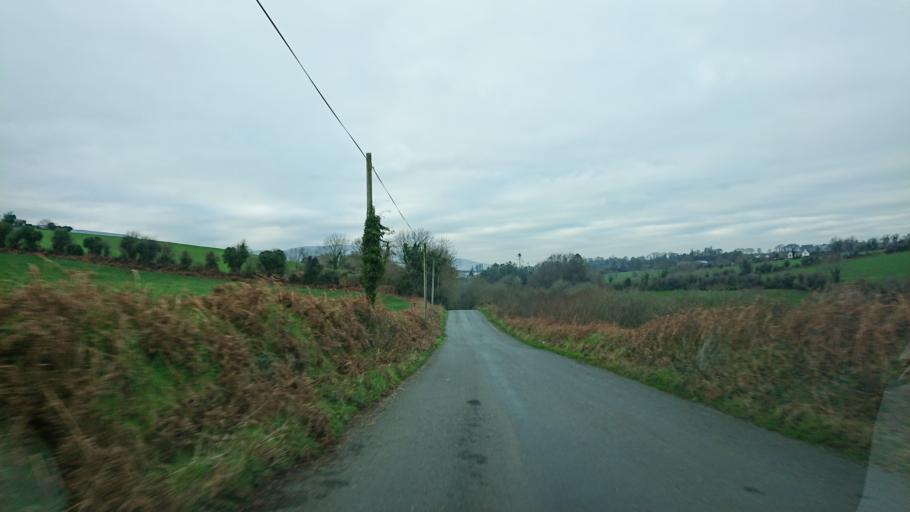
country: IE
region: Munster
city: Carrick-on-Suir
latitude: 52.2782
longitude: -7.4312
